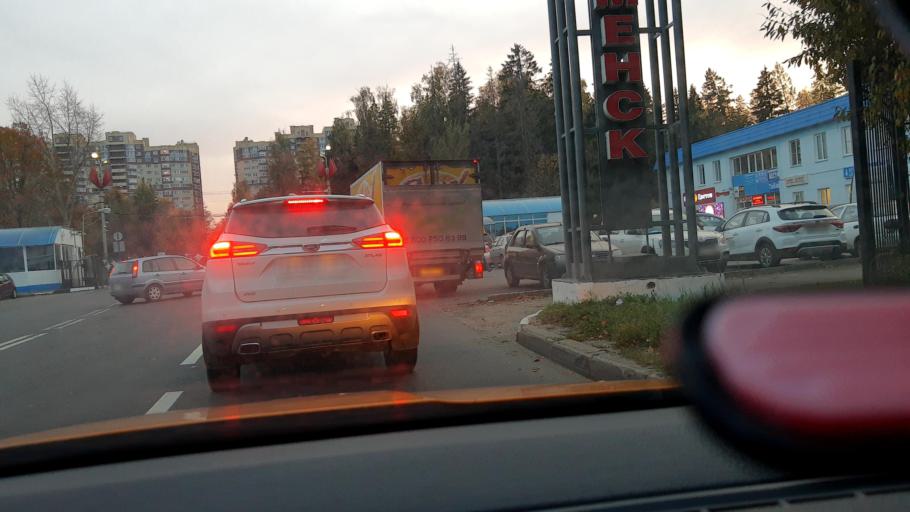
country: RU
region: Moskovskaya
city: Krasnoznamensk
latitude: 55.6038
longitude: 37.0488
